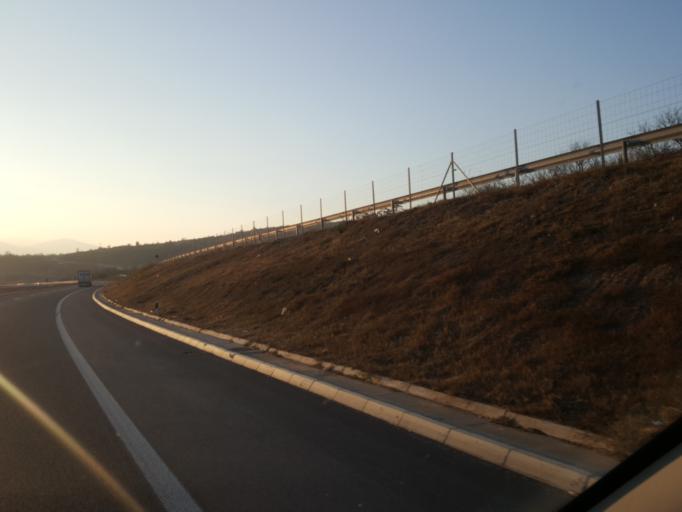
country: RS
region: Central Serbia
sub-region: Pirotski Okrug
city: Bela Palanka
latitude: 43.2314
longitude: 22.4440
